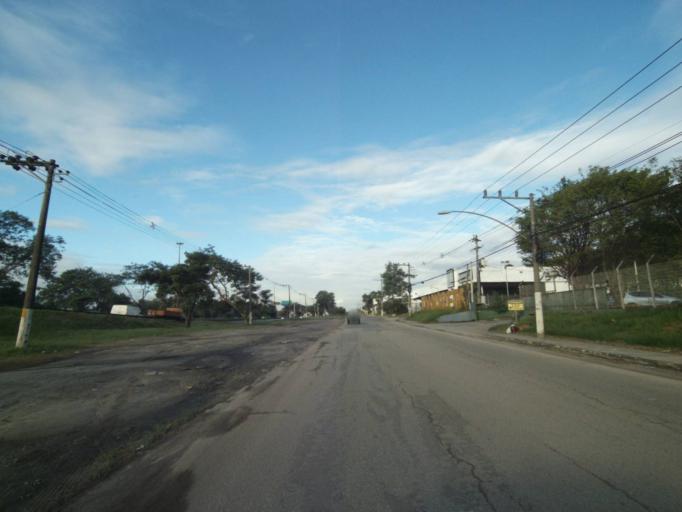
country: BR
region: Rio de Janeiro
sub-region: Nilopolis
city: Nilopolis
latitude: -22.8564
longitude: -43.4785
